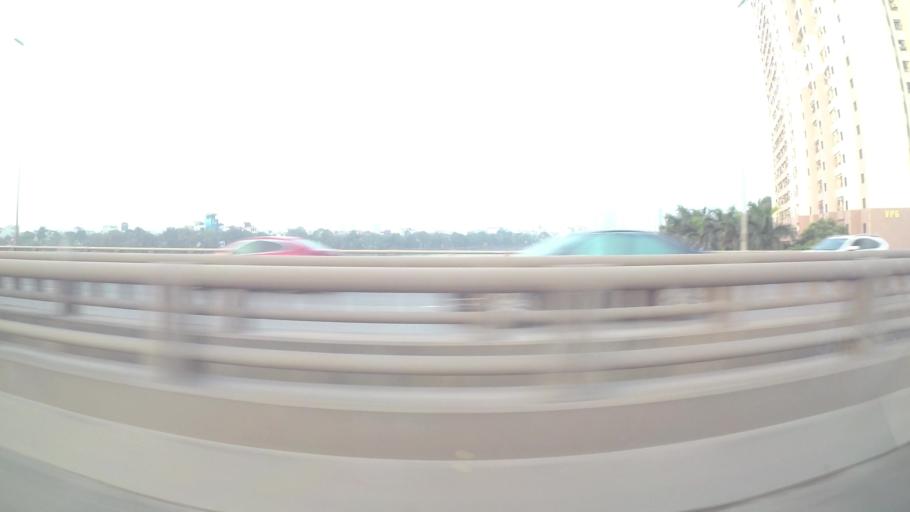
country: VN
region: Ha Noi
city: Van Dien
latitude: 20.9672
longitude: 105.8324
